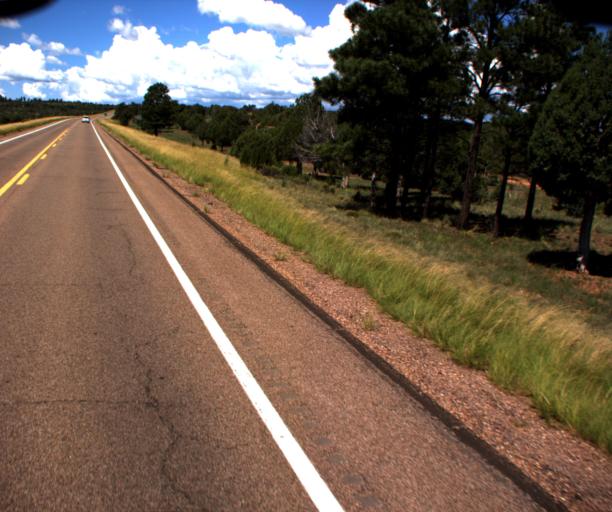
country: US
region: Arizona
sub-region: Navajo County
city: Linden
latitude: 34.3644
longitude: -110.3412
